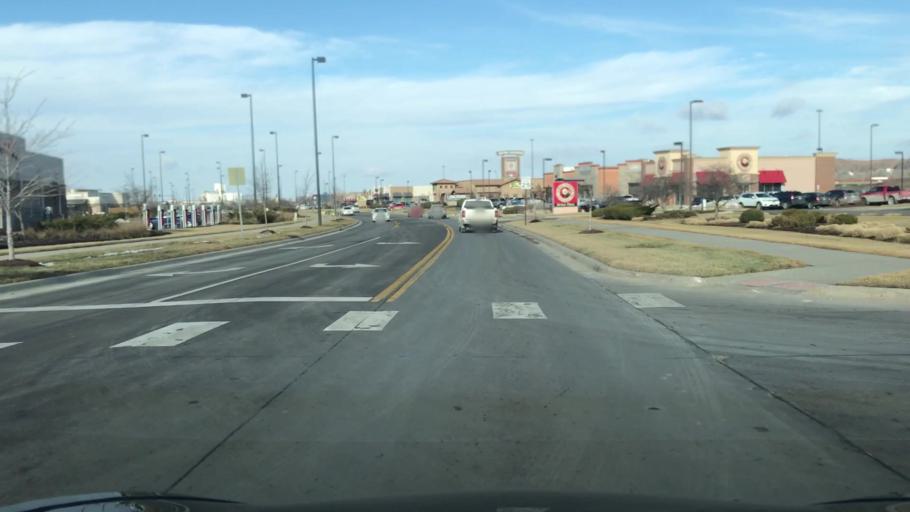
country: US
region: Iowa
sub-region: Pottawattamie County
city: Council Bluffs
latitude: 41.2205
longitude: -95.8352
